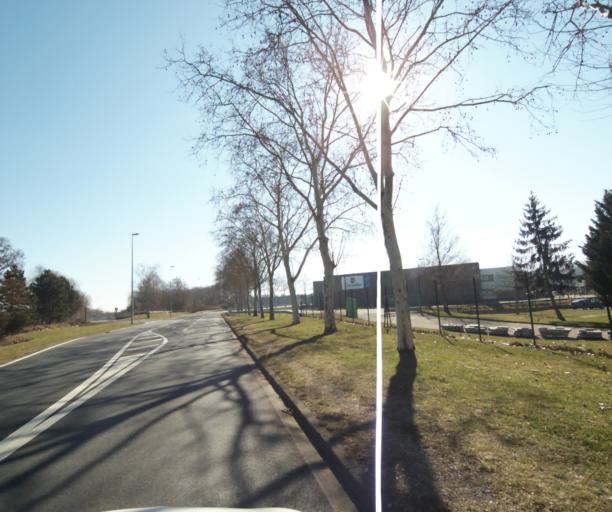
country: FR
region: Lorraine
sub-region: Departement de Meurthe-et-Moselle
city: Jarville-la-Malgrange
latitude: 48.6703
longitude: 6.2131
